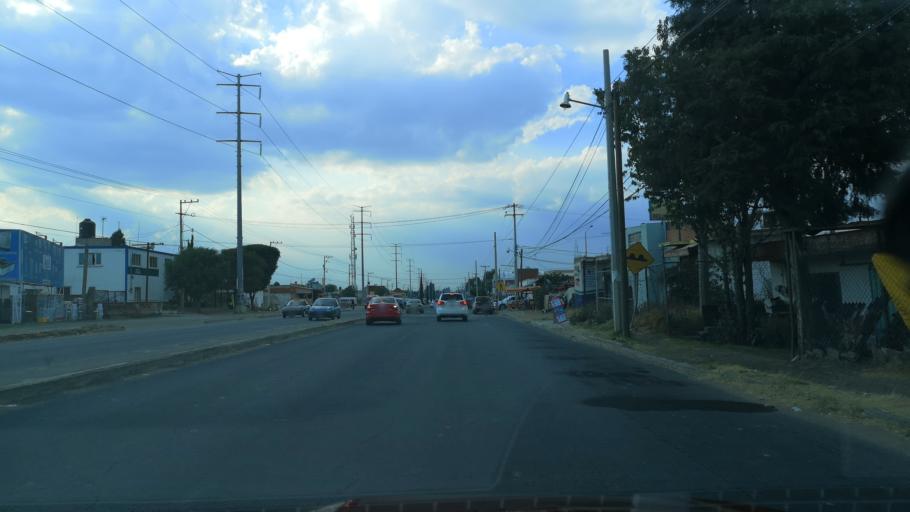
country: MX
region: Puebla
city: Cuanala
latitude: 19.0862
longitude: -98.3322
